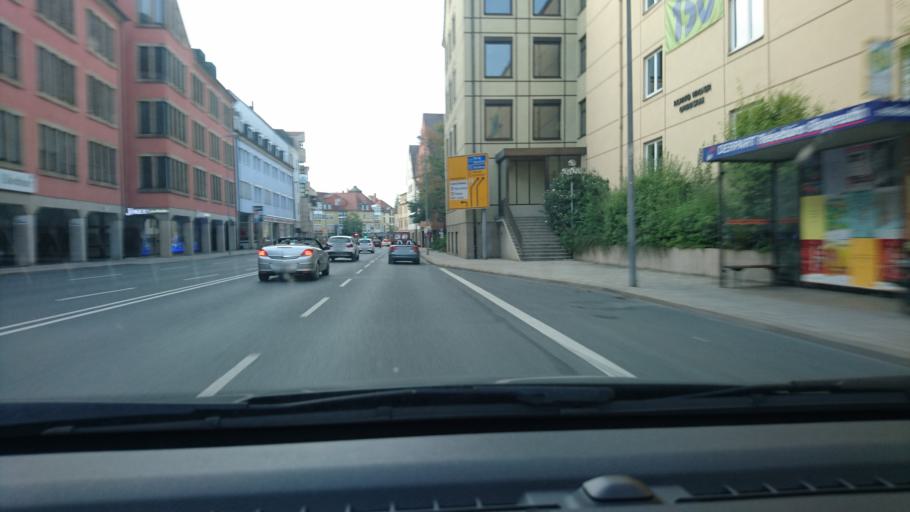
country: DE
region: Bavaria
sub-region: Upper Franconia
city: Bayreuth
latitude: 49.9422
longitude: 11.5708
